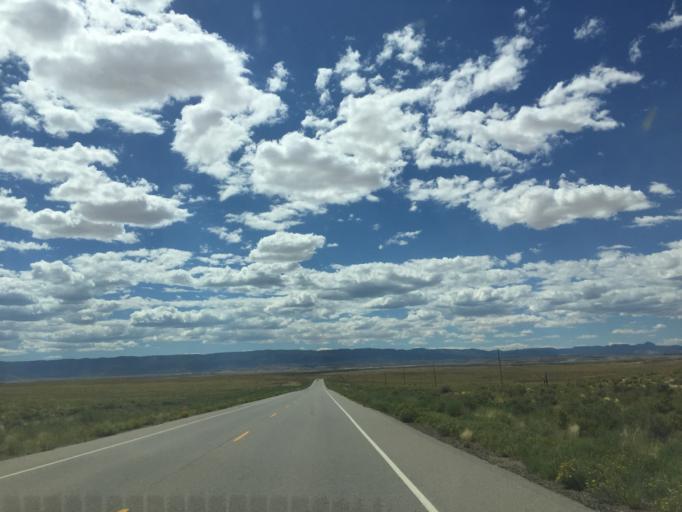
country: US
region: New Mexico
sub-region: San Juan County
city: Shiprock
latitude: 36.3441
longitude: -108.6775
